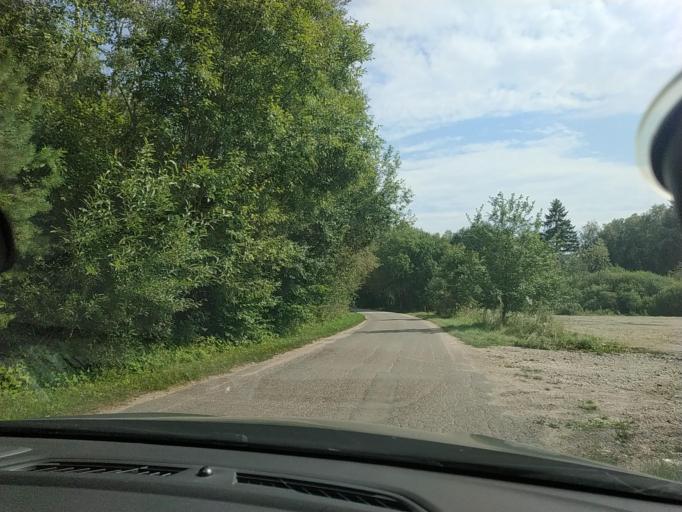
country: LT
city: Nemencine
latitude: 54.8475
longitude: 25.4548
